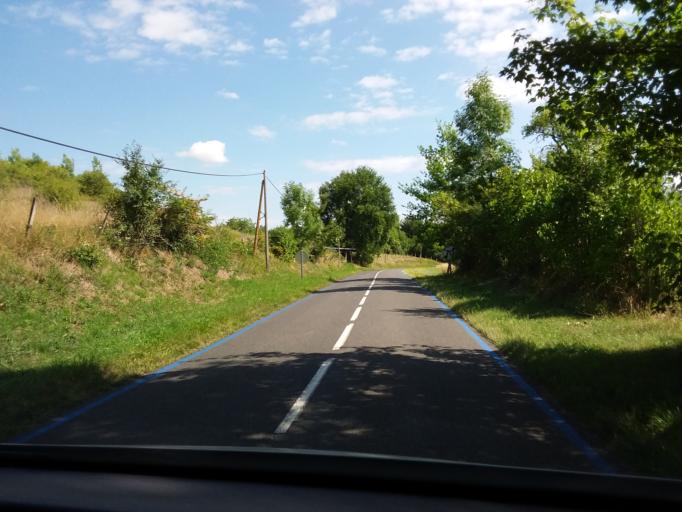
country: FR
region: Picardie
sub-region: Departement de l'Aisne
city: Saint-Erme-Outre-et-Ramecourt
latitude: 49.4460
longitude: 3.7928
